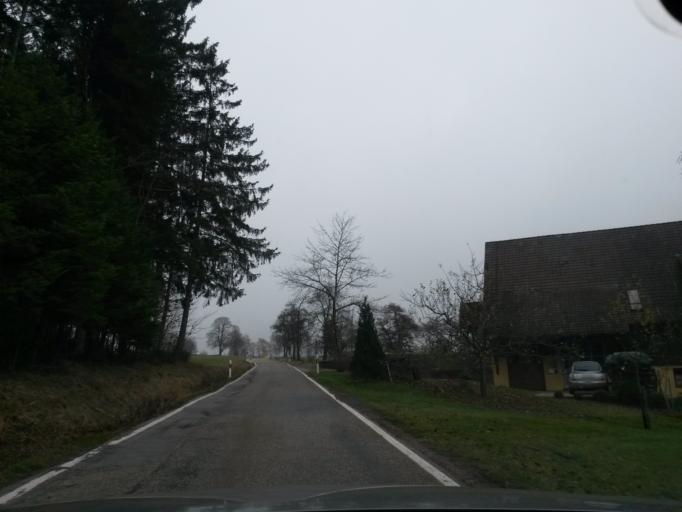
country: DE
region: Baden-Wuerttemberg
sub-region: Freiburg Region
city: Dornhan
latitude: 48.3536
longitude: 8.4655
